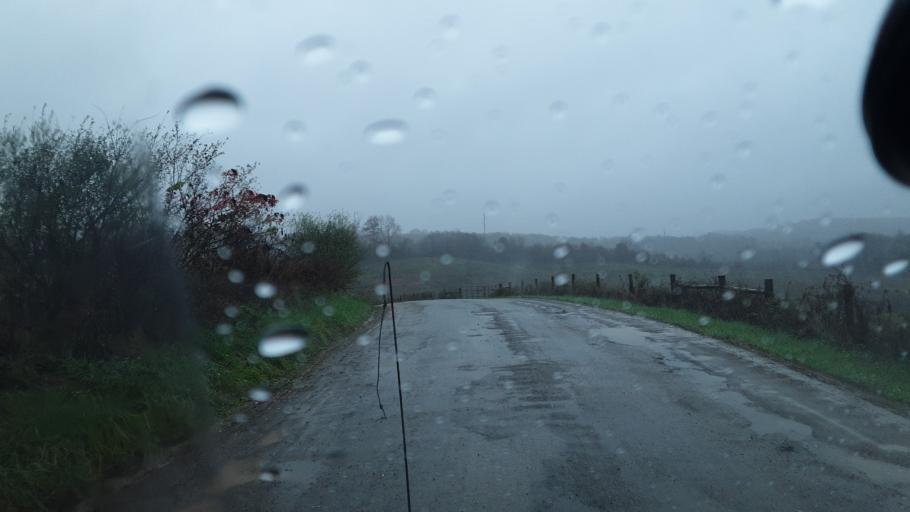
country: US
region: Ohio
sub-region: Vinton County
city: McArthur
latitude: 39.2251
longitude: -82.4677
